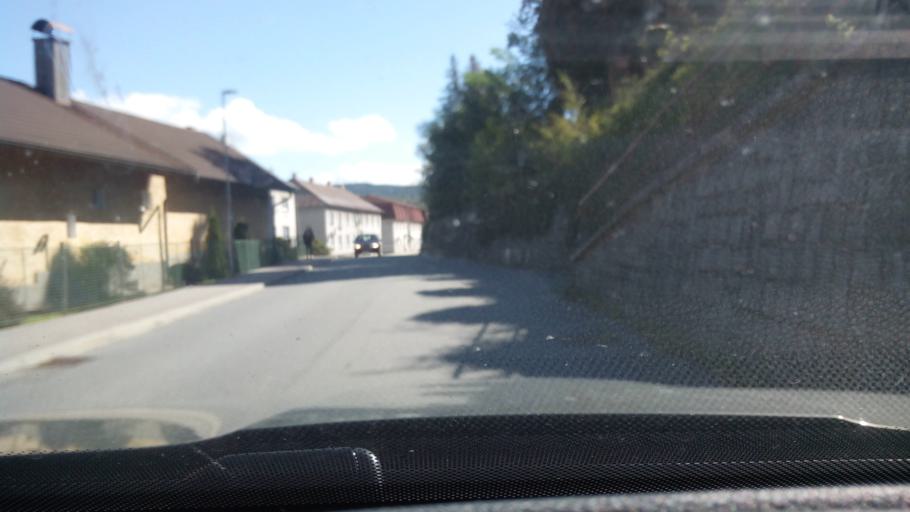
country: CZ
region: Jihocesky
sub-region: Okres Prachatice
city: Vimperk
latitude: 49.0578
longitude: 13.7774
